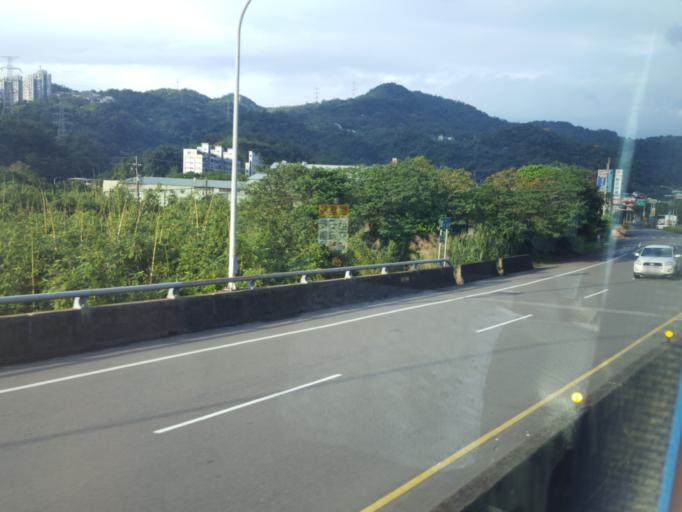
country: TW
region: Taipei
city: Taipei
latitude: 25.0046
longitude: 121.6302
